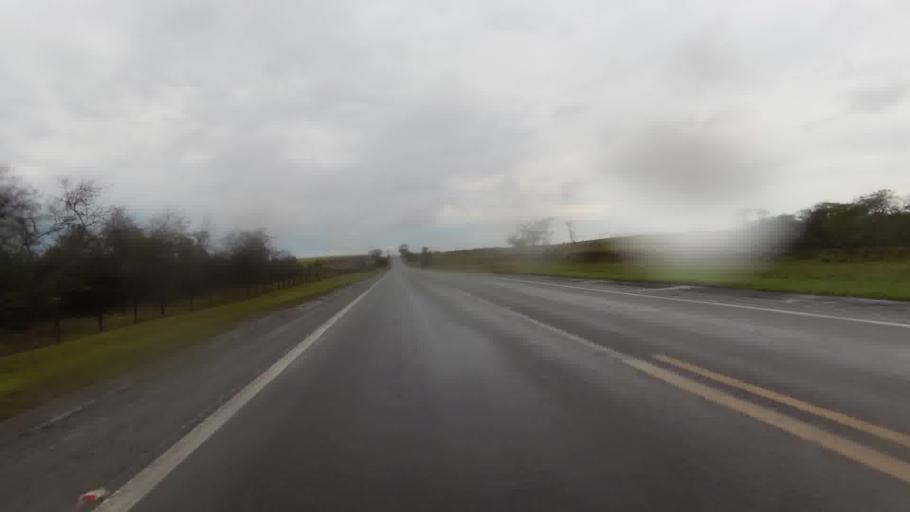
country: BR
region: Rio de Janeiro
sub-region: Campos Dos Goytacazes
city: Campos
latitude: -21.5192
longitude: -41.3341
